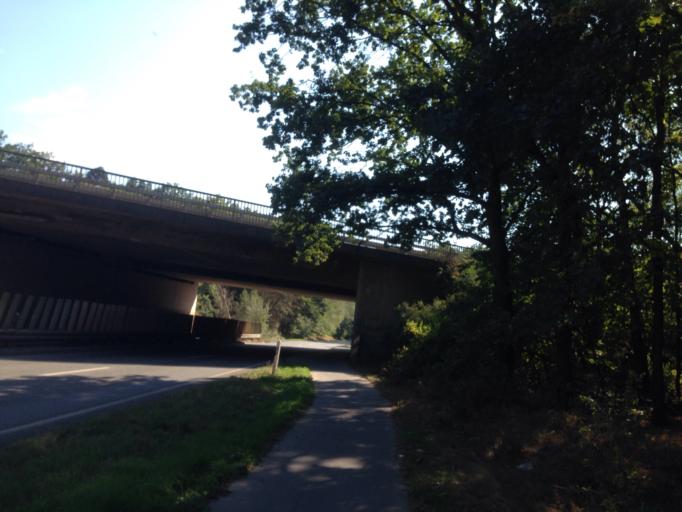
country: DE
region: Hesse
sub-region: Regierungsbezirk Giessen
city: Giessen
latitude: 50.5634
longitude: 8.6951
